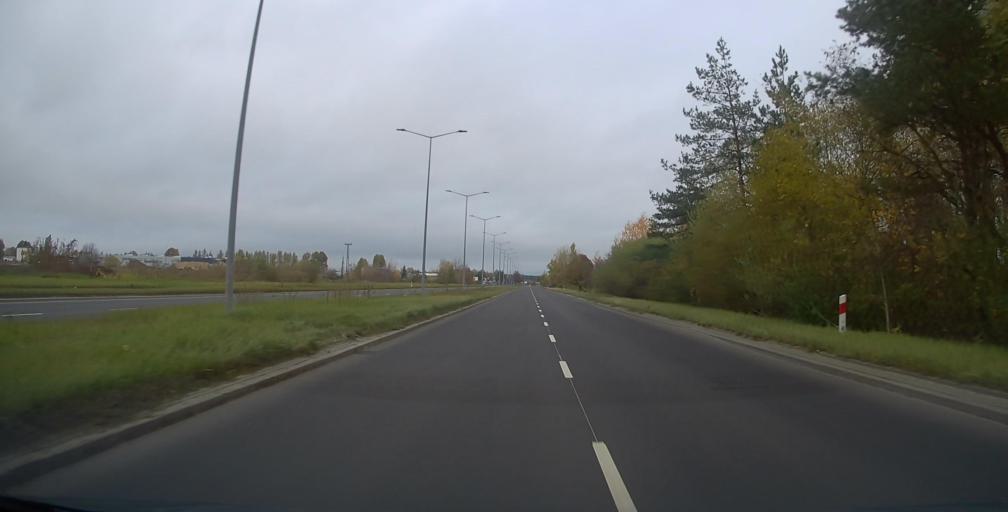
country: PL
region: Warmian-Masurian Voivodeship
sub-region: Powiat elcki
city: Elk
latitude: 53.8213
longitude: 22.3896
